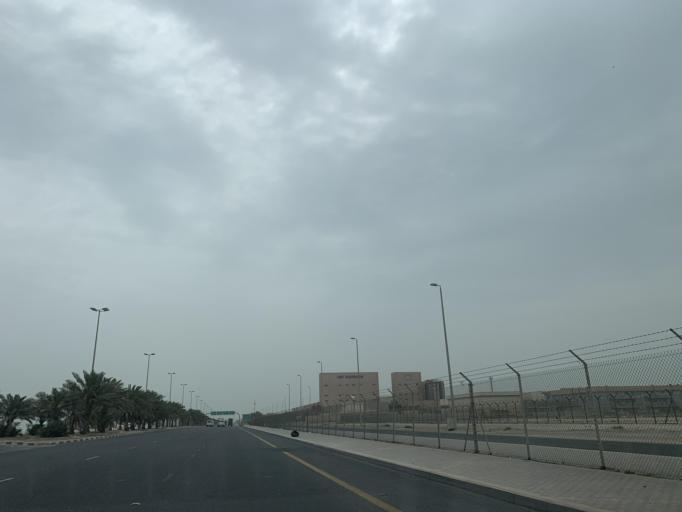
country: BH
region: Muharraq
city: Al Hadd
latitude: 26.2251
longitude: 50.6639
